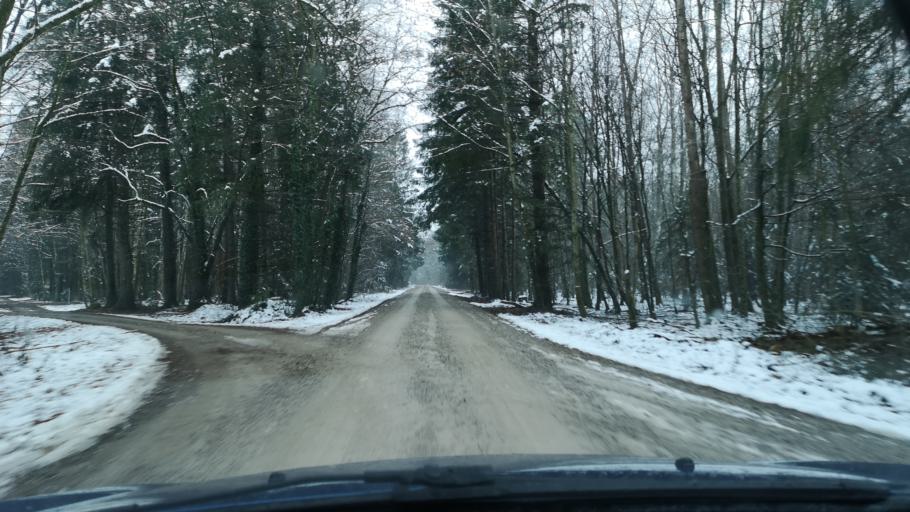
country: DE
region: Bavaria
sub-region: Upper Bavaria
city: Anzing
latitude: 48.1383
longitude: 11.8696
